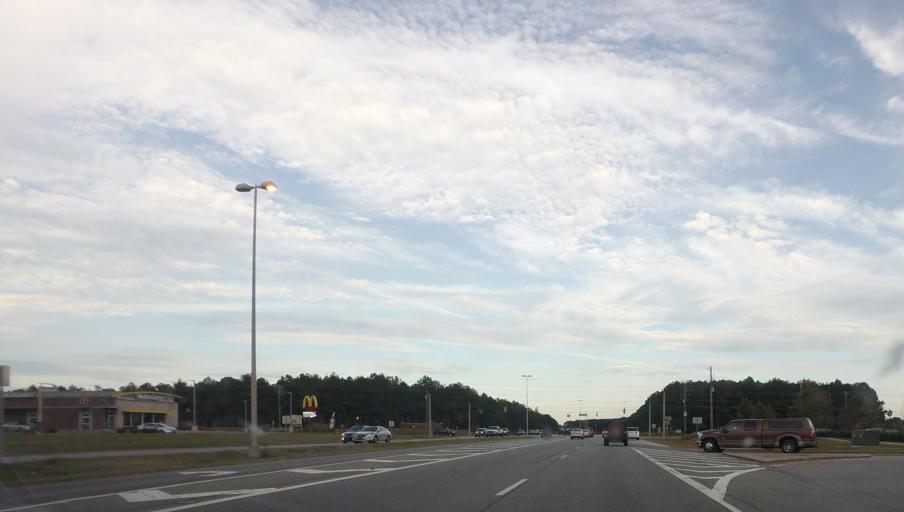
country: US
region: Georgia
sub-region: Houston County
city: Centerville
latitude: 32.5814
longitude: -83.6954
